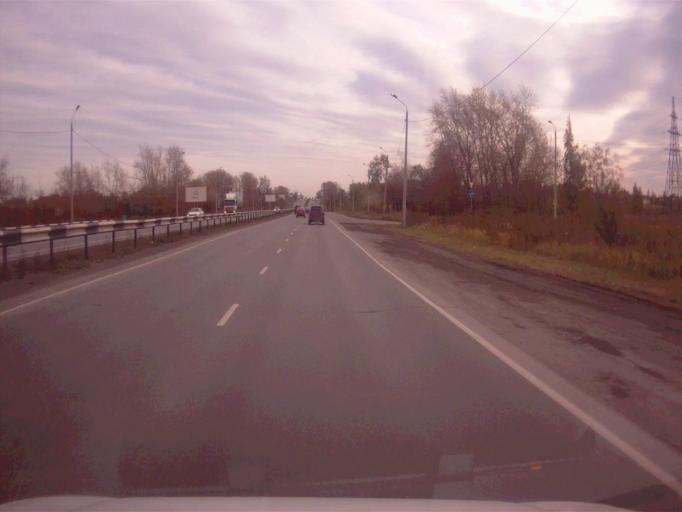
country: RU
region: Chelyabinsk
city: Novosineglazovskiy
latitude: 55.0609
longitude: 61.4013
